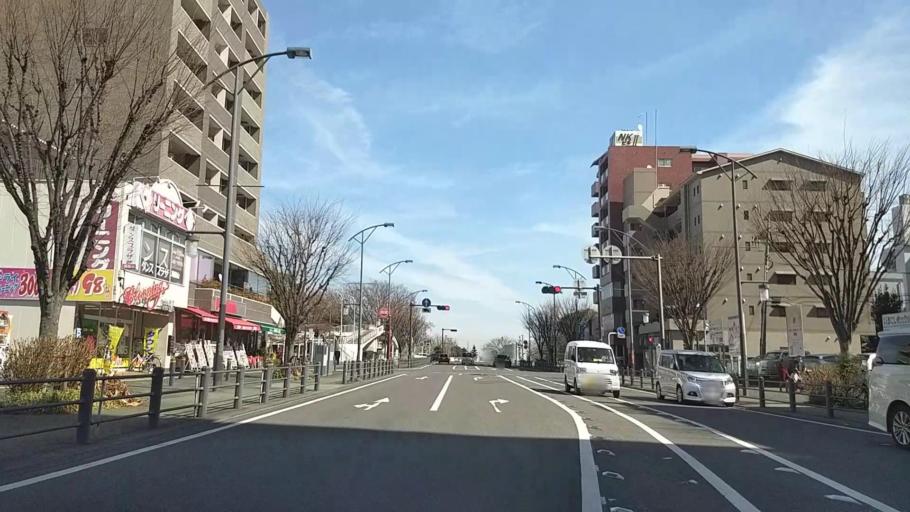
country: JP
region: Kanagawa
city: Fujisawa
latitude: 35.3969
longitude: 139.4690
